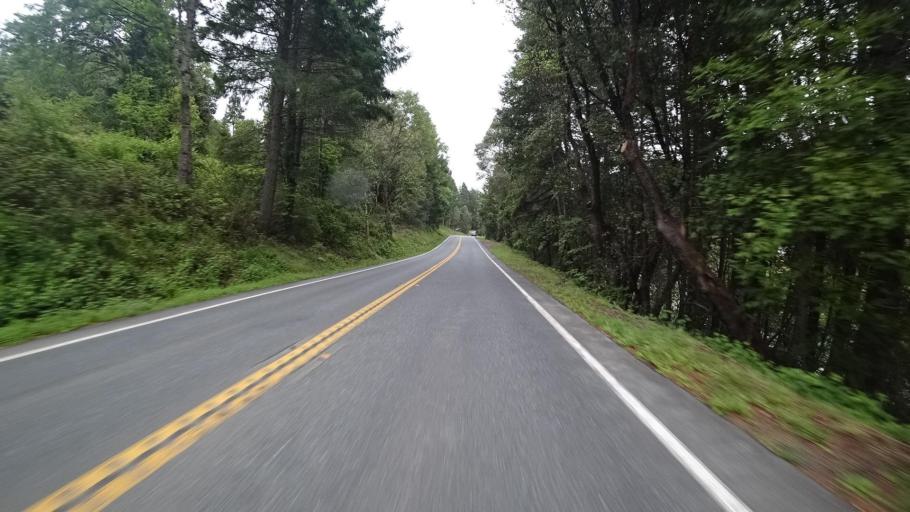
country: US
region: California
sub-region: Humboldt County
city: Willow Creek
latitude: 40.9657
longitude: -123.6415
